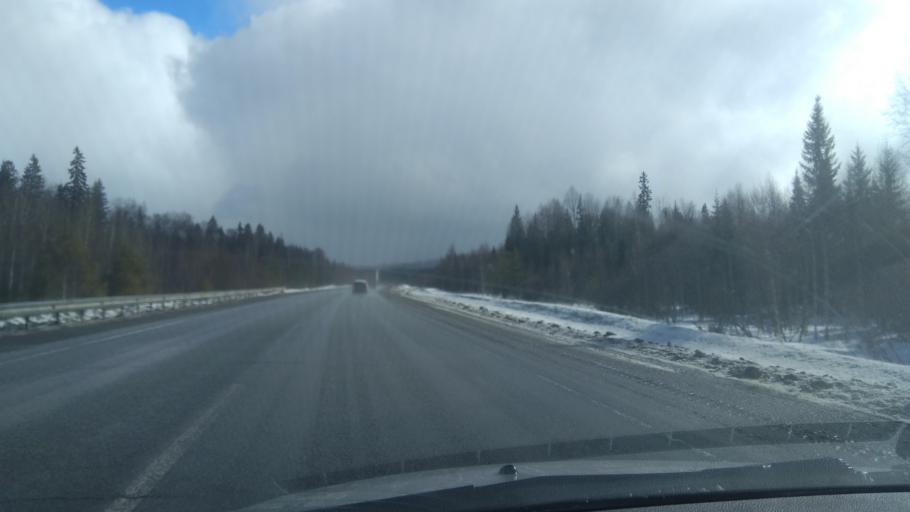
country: RU
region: Sverdlovsk
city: Arti
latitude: 56.7936
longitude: 58.4898
